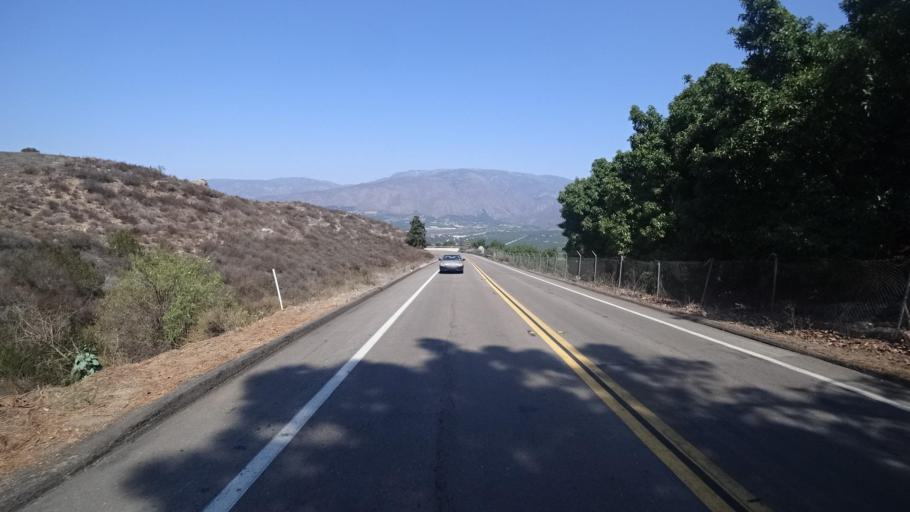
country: US
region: California
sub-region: San Diego County
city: Valley Center
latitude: 33.3038
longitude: -117.0121
